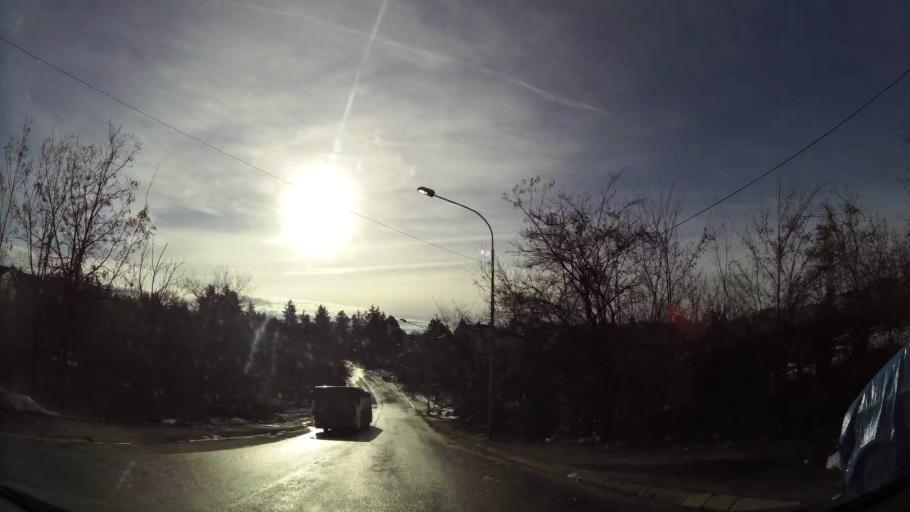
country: RS
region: Central Serbia
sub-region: Belgrade
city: Rakovica
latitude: 44.7222
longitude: 20.4286
